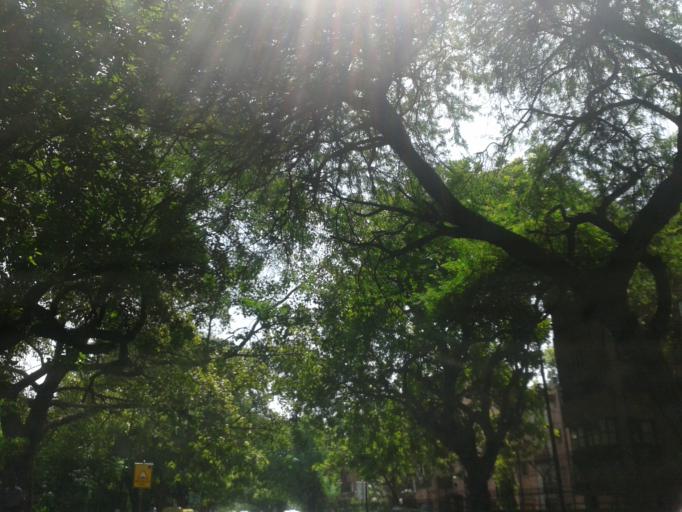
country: IN
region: NCT
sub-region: Central Delhi
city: Karol Bagh
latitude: 28.6315
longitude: 77.1987
